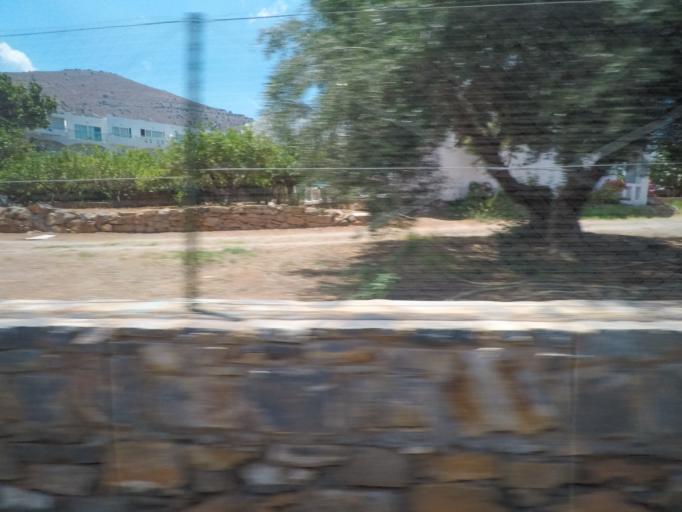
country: GR
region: Crete
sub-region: Nomos Lasithiou
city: Skhisma
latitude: 35.2461
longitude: 25.7298
